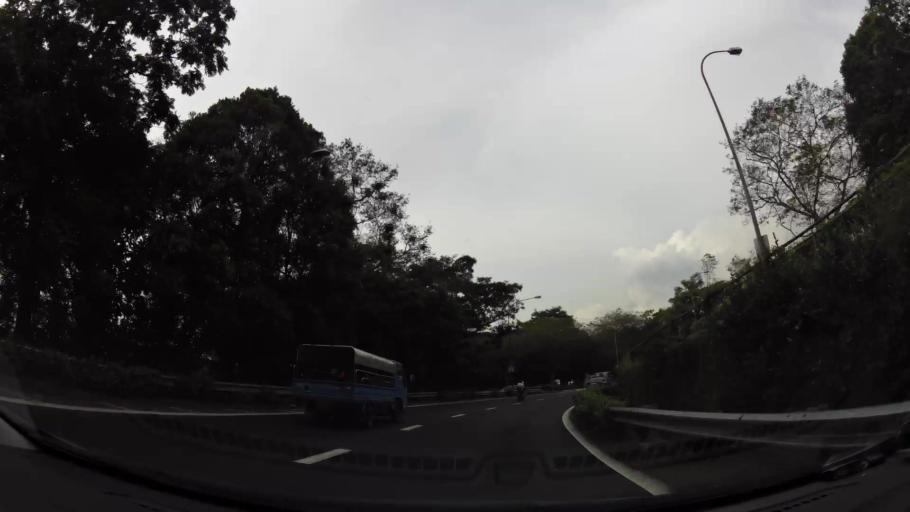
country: MY
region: Johor
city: Johor Bahru
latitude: 1.4200
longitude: 103.7698
